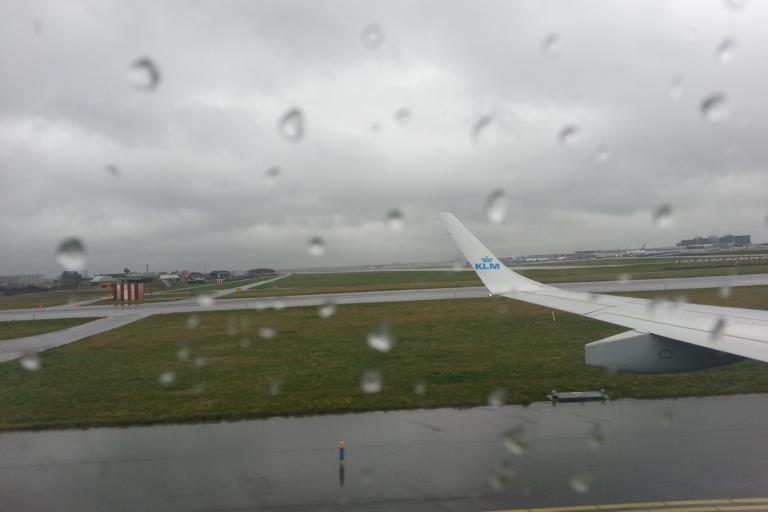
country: NL
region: North Holland
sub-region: Gemeente Haarlemmermeer
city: Hoofddorp
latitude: 52.3178
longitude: 4.7415
